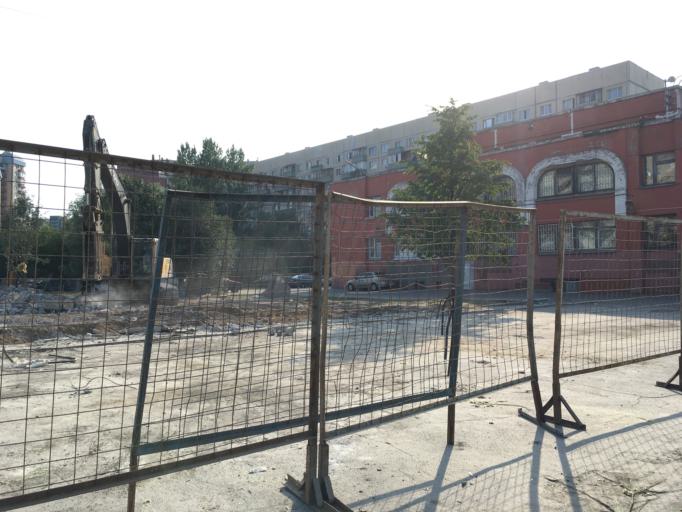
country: RU
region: St.-Petersburg
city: Komendantsky aerodrom
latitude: 60.0165
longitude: 30.2556
